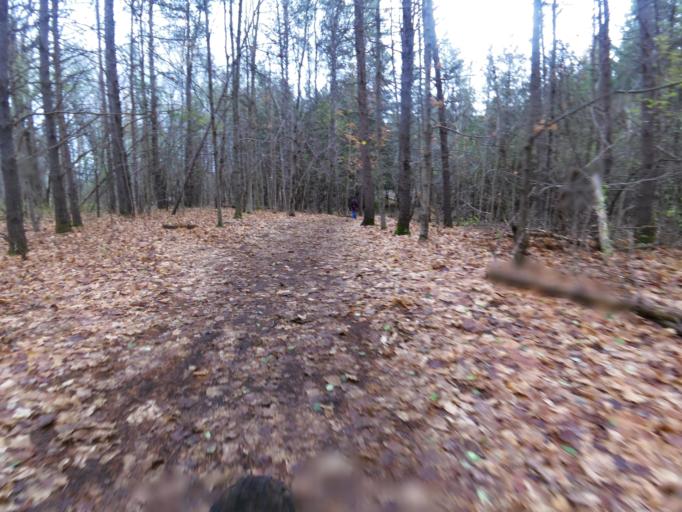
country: CA
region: Ontario
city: Bells Corners
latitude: 45.3045
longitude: -75.8138
